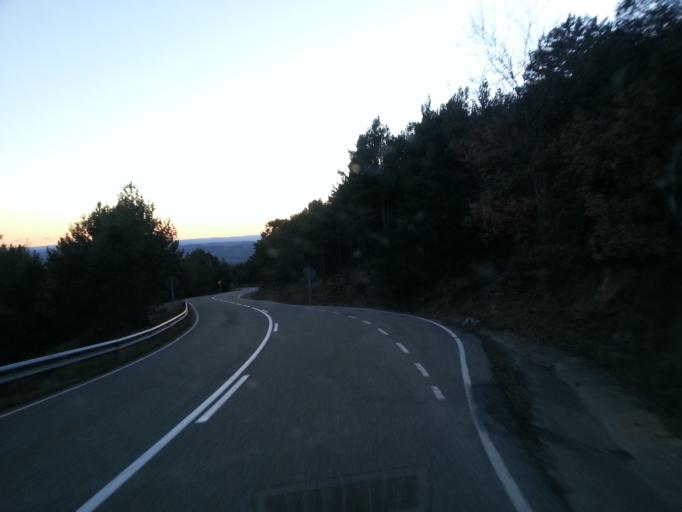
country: ES
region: Catalonia
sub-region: Provincia de Lleida
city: Olius
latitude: 42.0892
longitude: 1.5258
